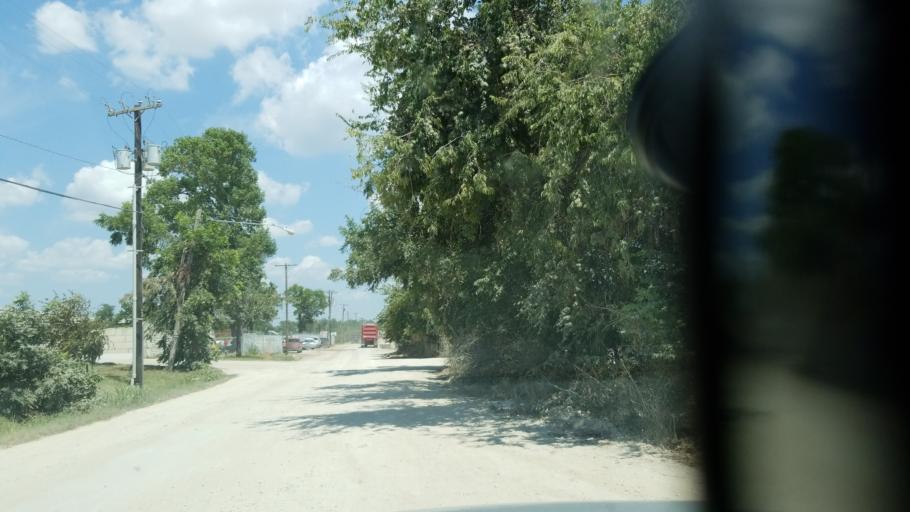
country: US
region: Texas
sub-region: Dallas County
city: Farmers Branch
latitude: 32.8761
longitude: -96.9192
